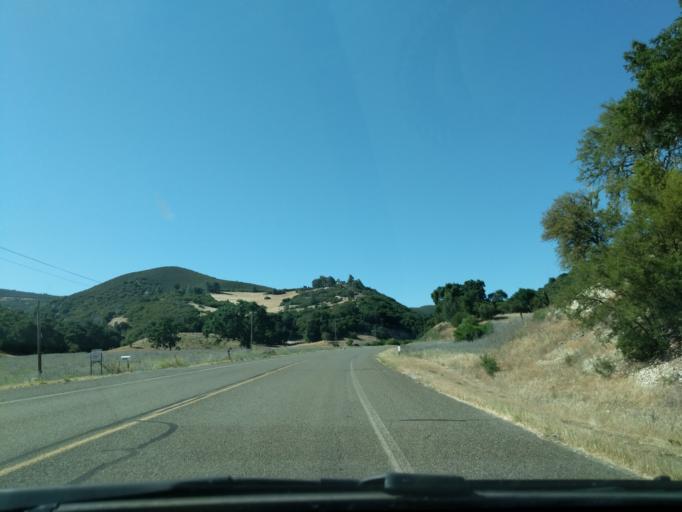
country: US
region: California
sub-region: Monterey County
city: King City
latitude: 36.0612
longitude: -121.1847
